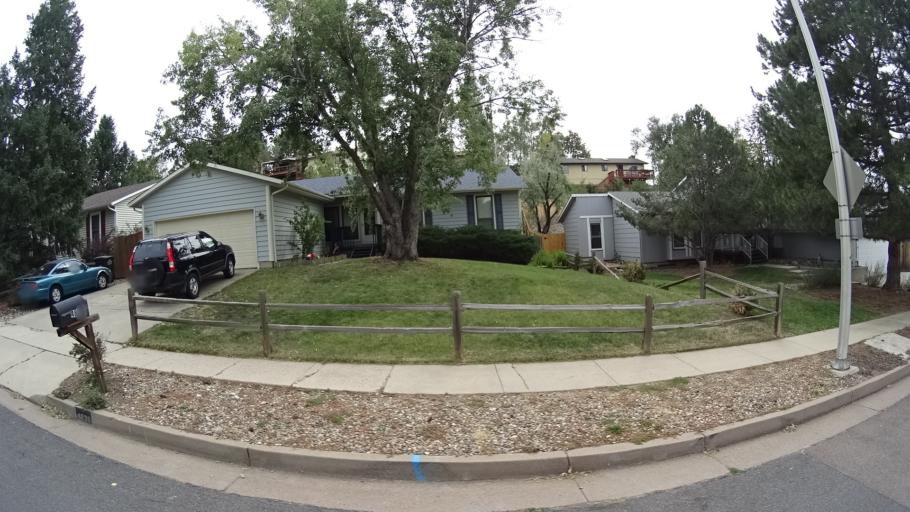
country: US
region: Colorado
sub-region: El Paso County
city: Cimarron Hills
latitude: 38.9011
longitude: -104.7315
